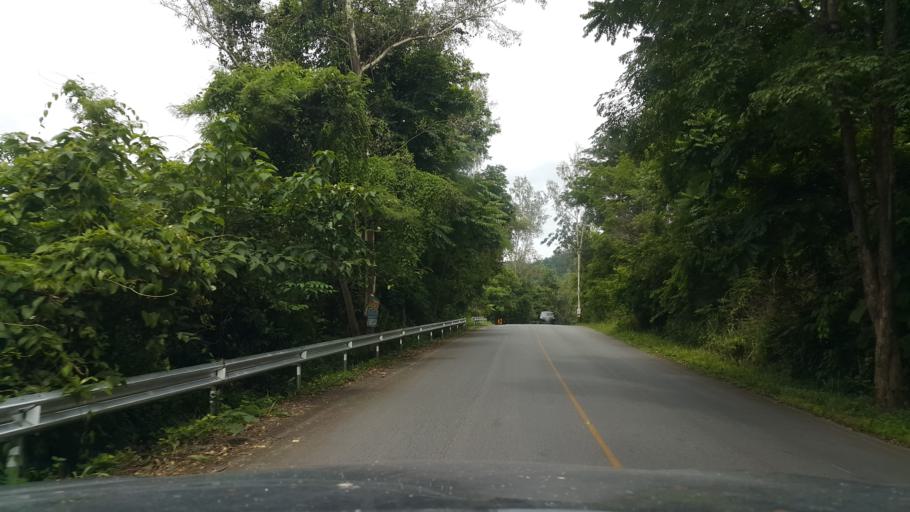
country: TH
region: Lampang
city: Thoen
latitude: 17.5995
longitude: 99.3307
